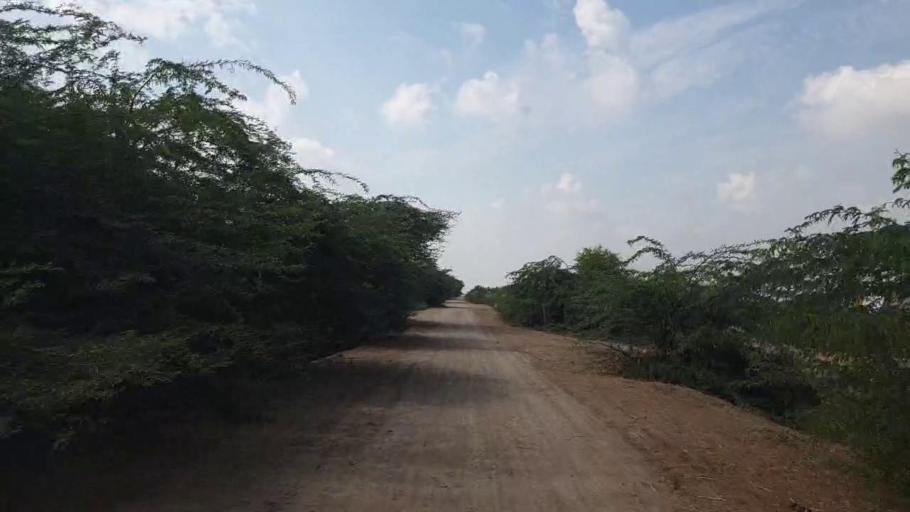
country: PK
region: Sindh
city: Badin
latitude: 24.5066
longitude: 68.6428
